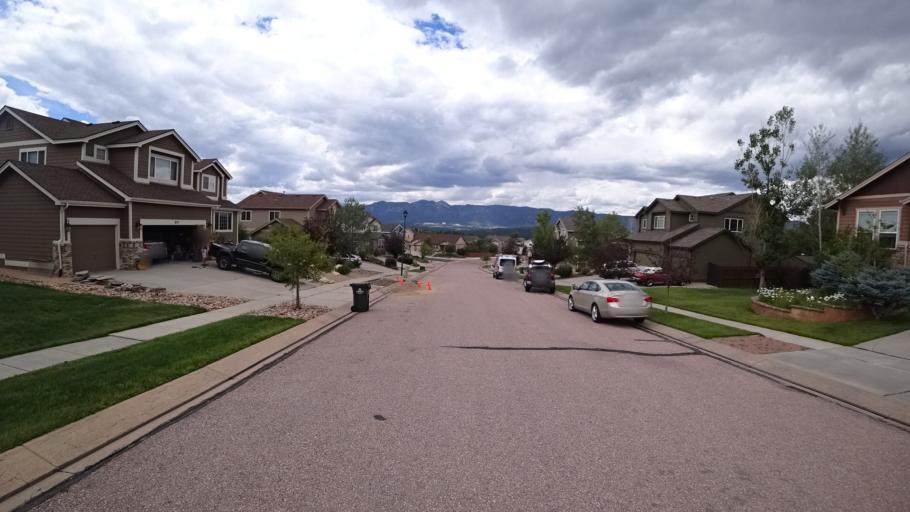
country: US
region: Colorado
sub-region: El Paso County
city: Gleneagle
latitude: 39.0340
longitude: -104.8115
